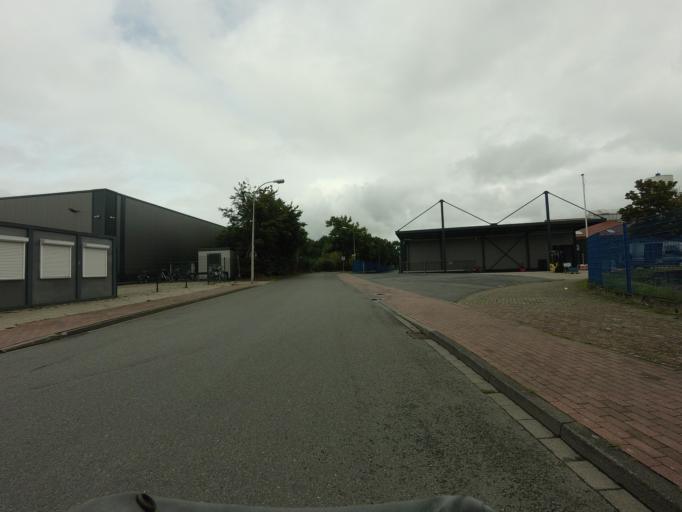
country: DE
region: North Rhine-Westphalia
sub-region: Regierungsbezirk Munster
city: Gronau
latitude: 52.2180
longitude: 7.0234
